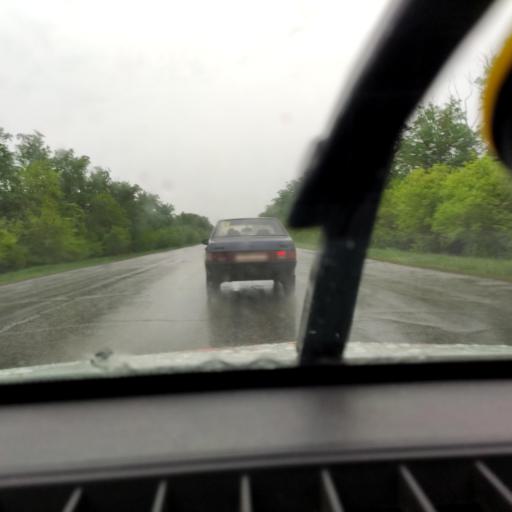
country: RU
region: Samara
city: Tol'yatti
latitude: 53.6177
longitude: 49.4137
